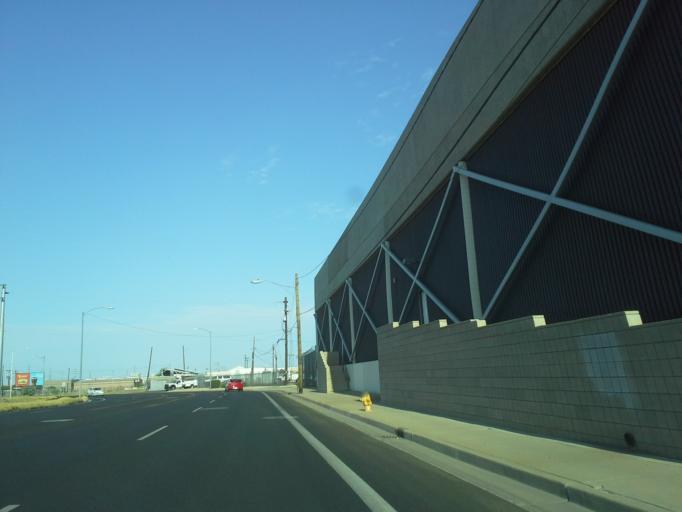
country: US
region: Arizona
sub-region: Maricopa County
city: Phoenix
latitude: 33.4422
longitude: -112.0785
